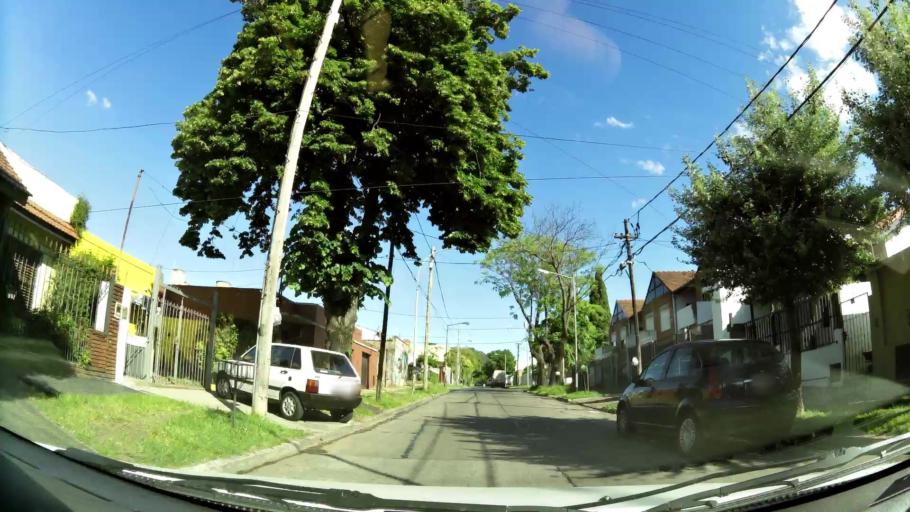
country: AR
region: Buenos Aires
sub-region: Partido de General San Martin
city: General San Martin
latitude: -34.5372
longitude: -58.5676
